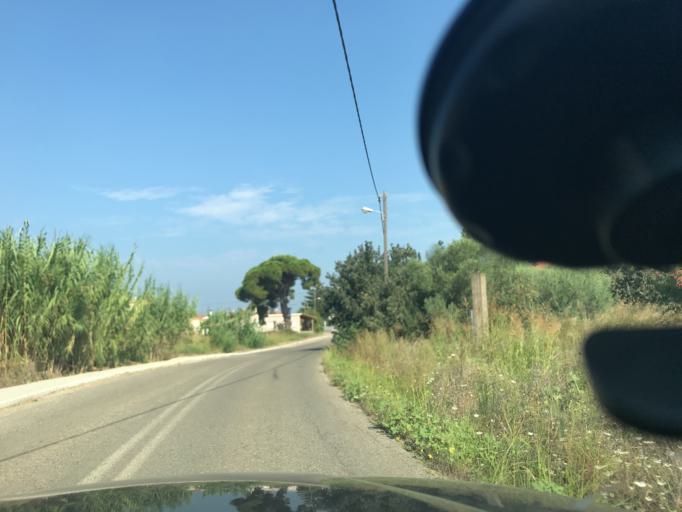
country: GR
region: West Greece
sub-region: Nomos Ileias
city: Kardamas
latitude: 37.7166
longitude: 21.3333
